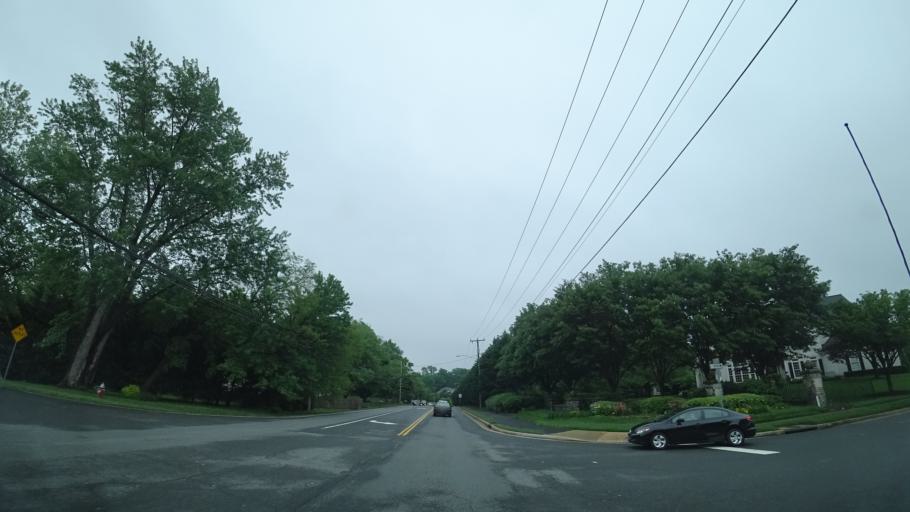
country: US
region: Virginia
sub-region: Fairfax County
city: Tysons Corner
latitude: 38.9391
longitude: -77.2435
